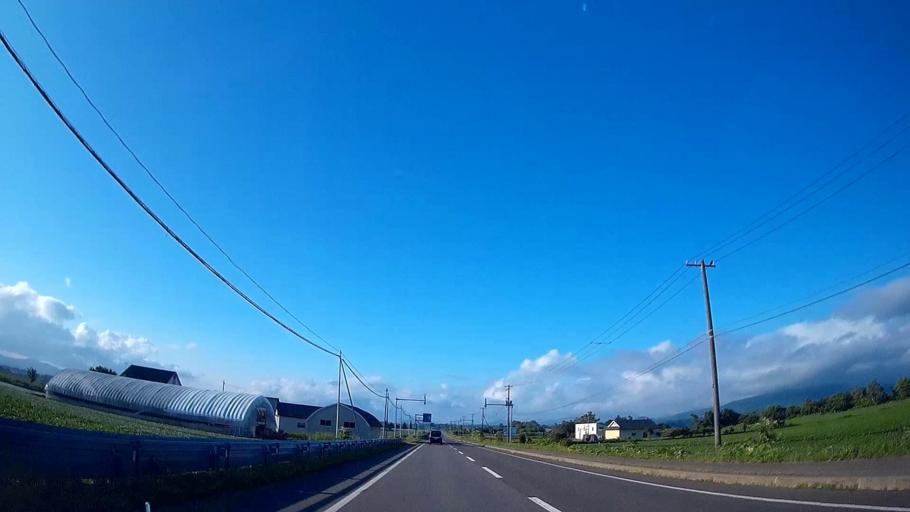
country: JP
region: Hokkaido
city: Date
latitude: 42.6392
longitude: 140.8024
